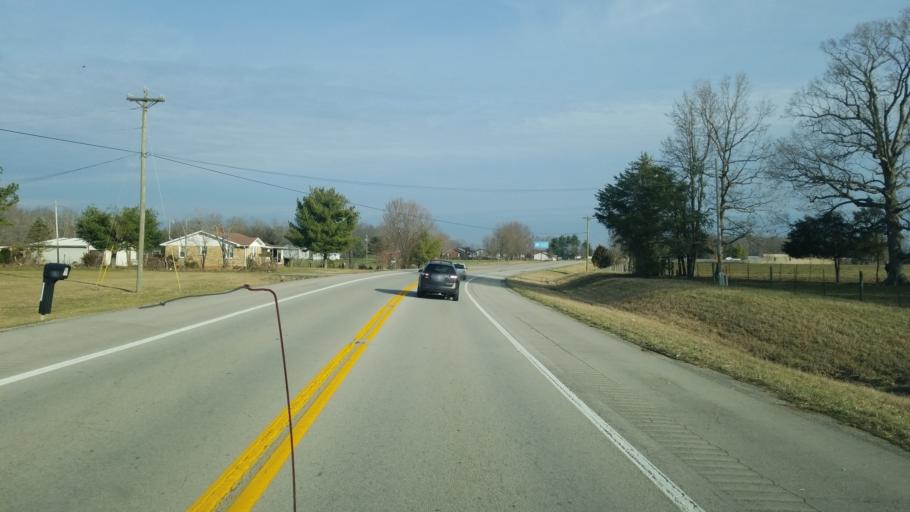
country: US
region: Kentucky
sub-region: Russell County
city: Russell Springs
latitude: 37.1349
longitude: -85.0342
